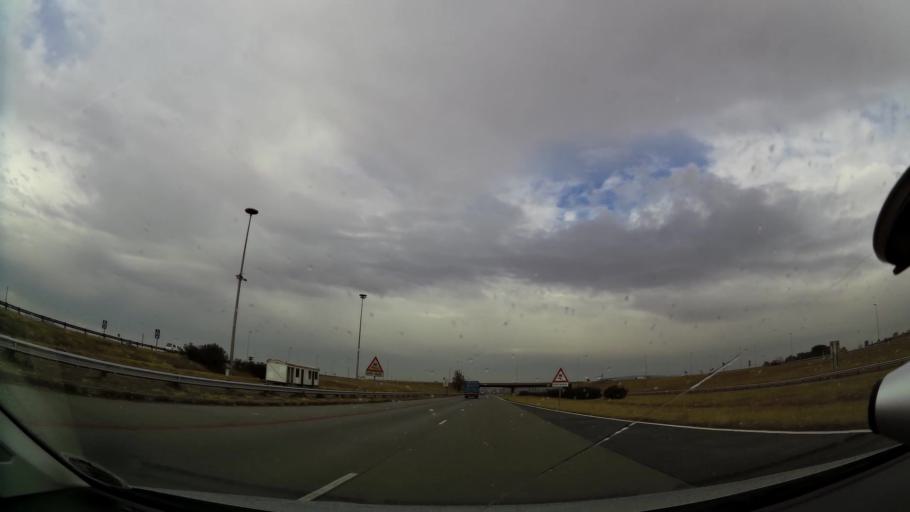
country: ZA
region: Gauteng
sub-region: City of Johannesburg Metropolitan Municipality
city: Orange Farm
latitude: -26.4135
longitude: 27.8827
